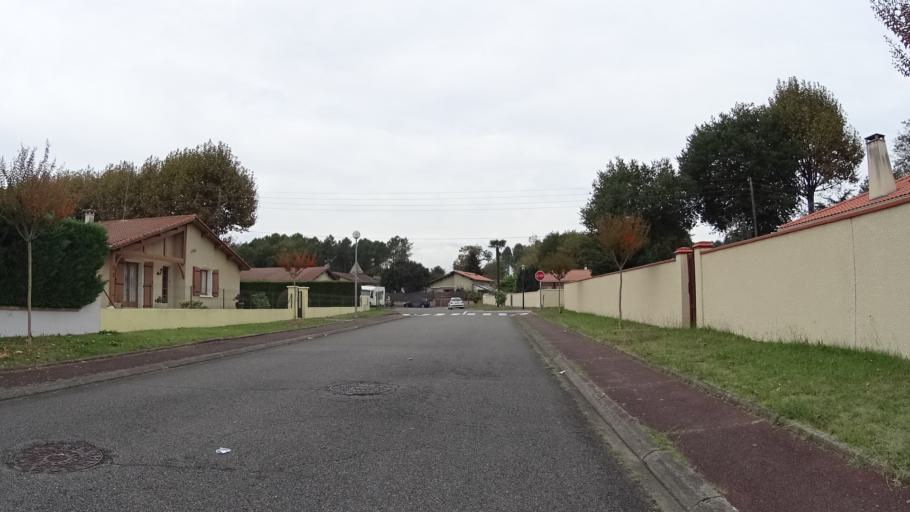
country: FR
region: Aquitaine
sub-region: Departement des Landes
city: Mees
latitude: 43.7303
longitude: -1.0864
